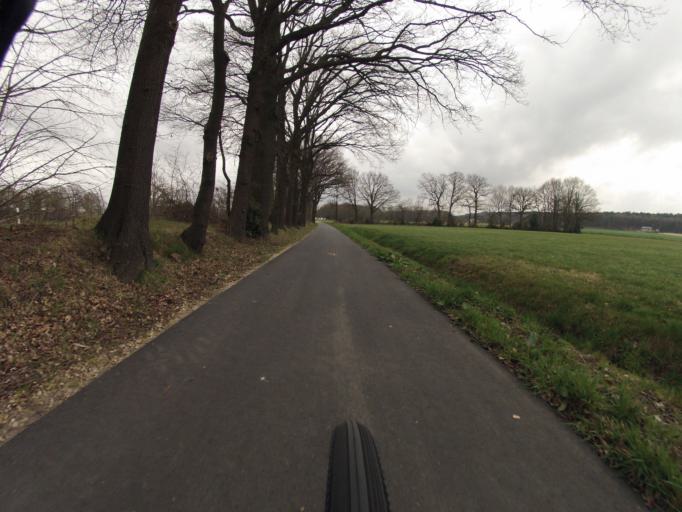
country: DE
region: North Rhine-Westphalia
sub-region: Regierungsbezirk Munster
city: Recke
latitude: 52.3449
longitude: 7.7150
